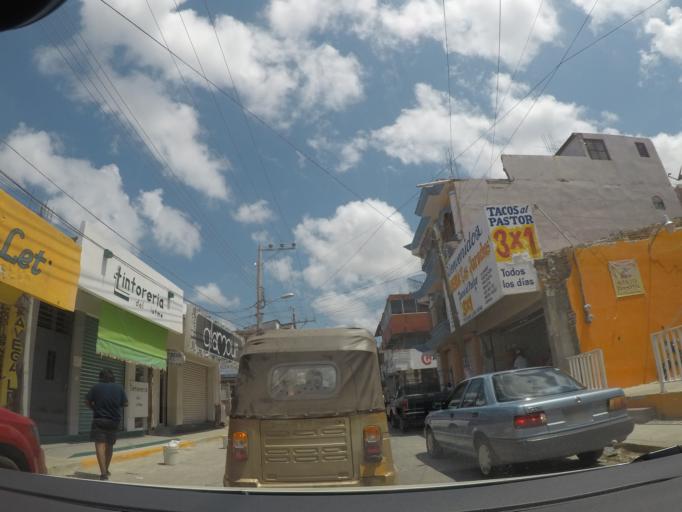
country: MX
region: Oaxaca
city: Juchitan de Zaragoza
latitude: 16.4354
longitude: -95.0224
